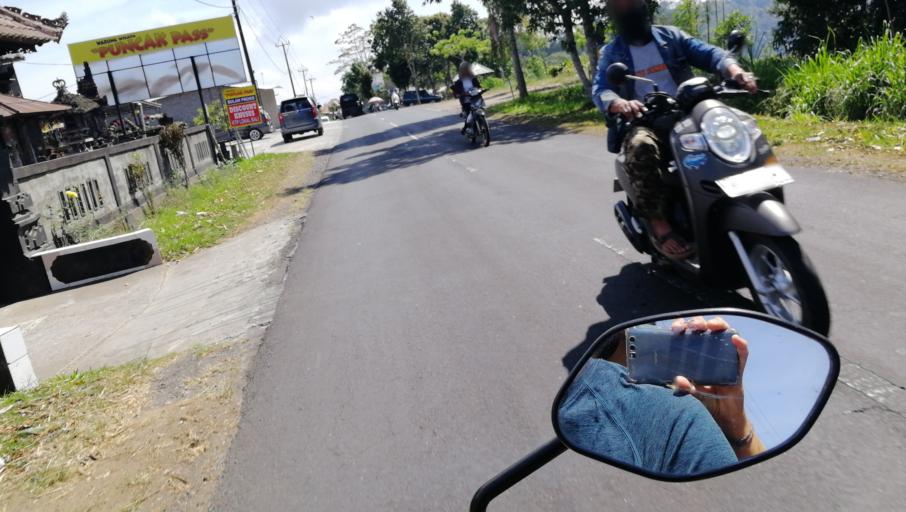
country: ID
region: Bali
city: Munduk
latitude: -8.2408
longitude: 115.1066
